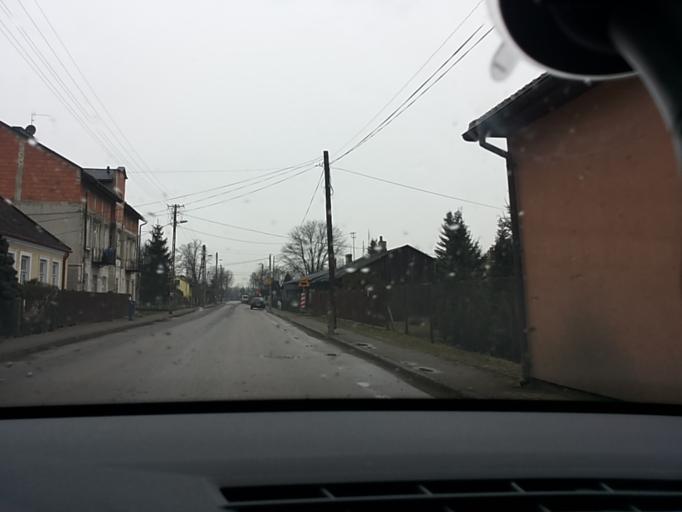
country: PL
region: Lodz Voivodeship
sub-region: Skierniewice
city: Skierniewice
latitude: 51.9623
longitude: 20.1353
